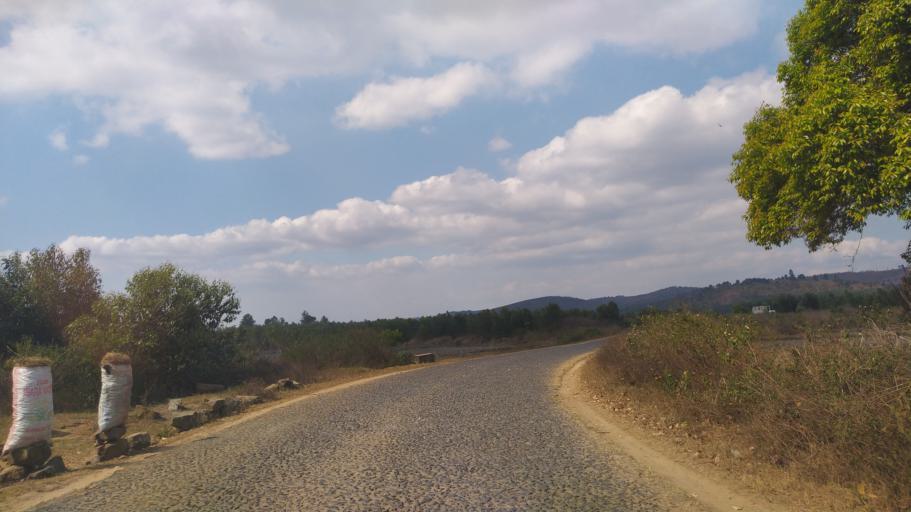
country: MG
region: Alaotra Mangoro
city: Moramanga
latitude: -18.7687
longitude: 48.2518
